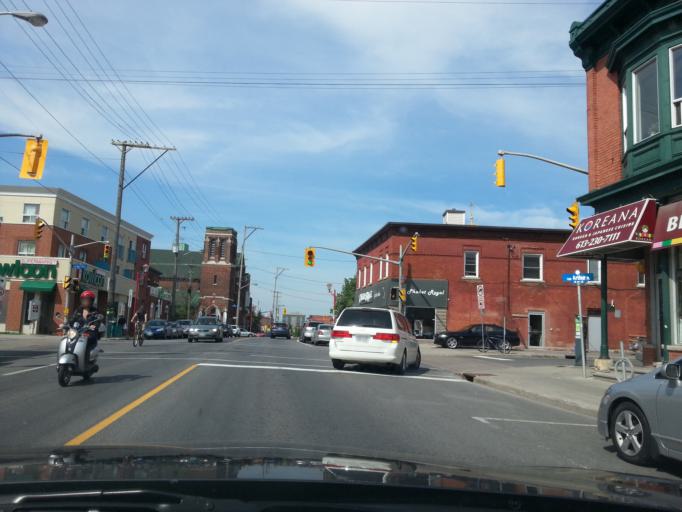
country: CA
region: Ontario
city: Ottawa
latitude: 45.4109
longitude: -75.7072
